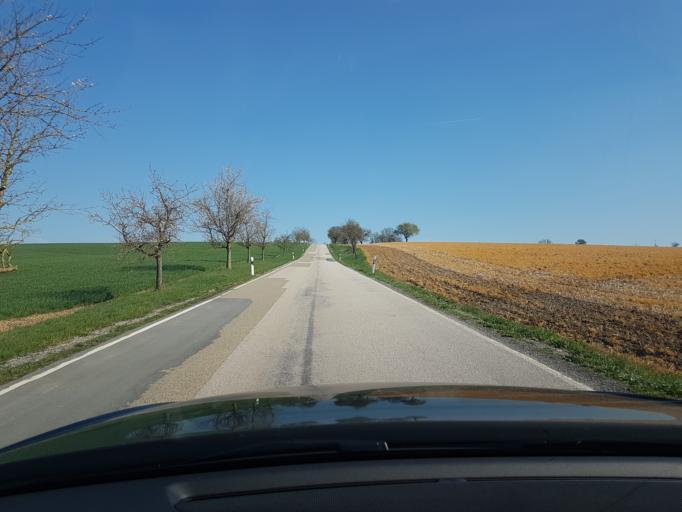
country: DE
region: Baden-Wuerttemberg
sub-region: Regierungsbezirk Stuttgart
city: Jagsthausen
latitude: 49.2956
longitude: 9.4744
